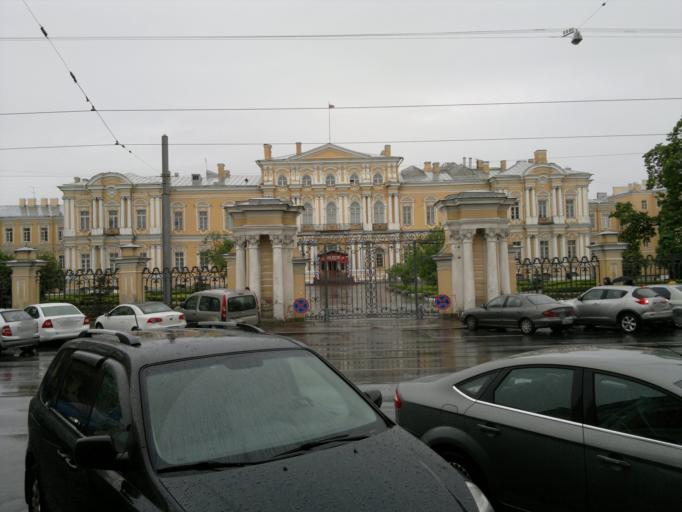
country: RU
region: St.-Petersburg
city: Saint Petersburg
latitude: 59.9322
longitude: 30.3304
